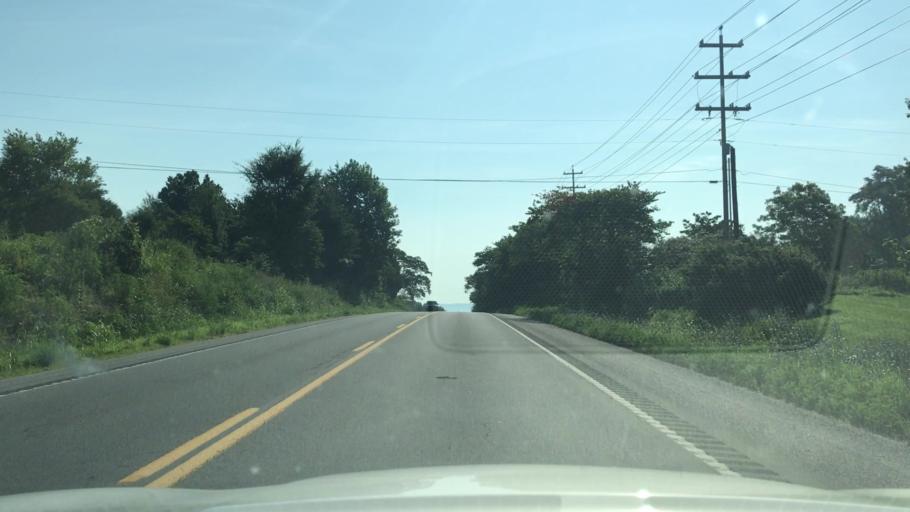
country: US
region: Tennessee
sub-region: Overton County
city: Livingston
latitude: 36.4405
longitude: -85.2442
